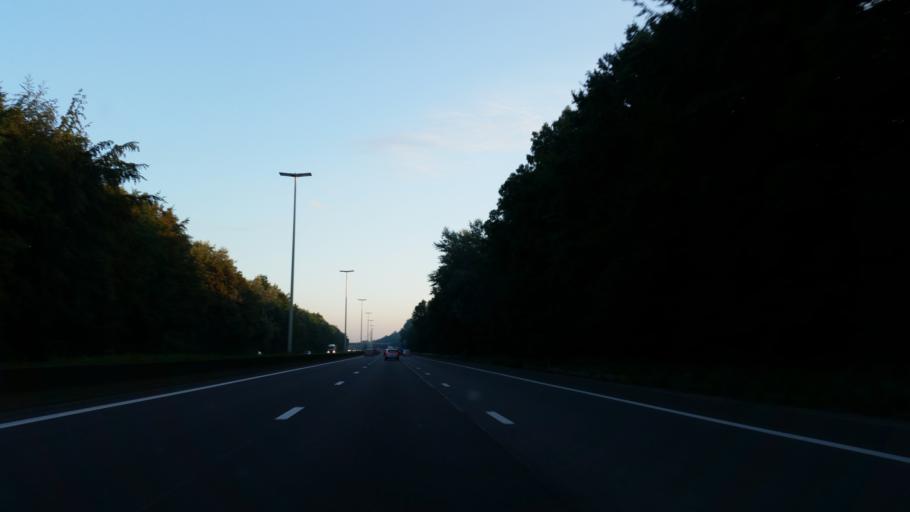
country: BE
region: Wallonia
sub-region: Province du Brabant Wallon
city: Louvain-la-Neuve
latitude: 50.6854
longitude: 4.6245
